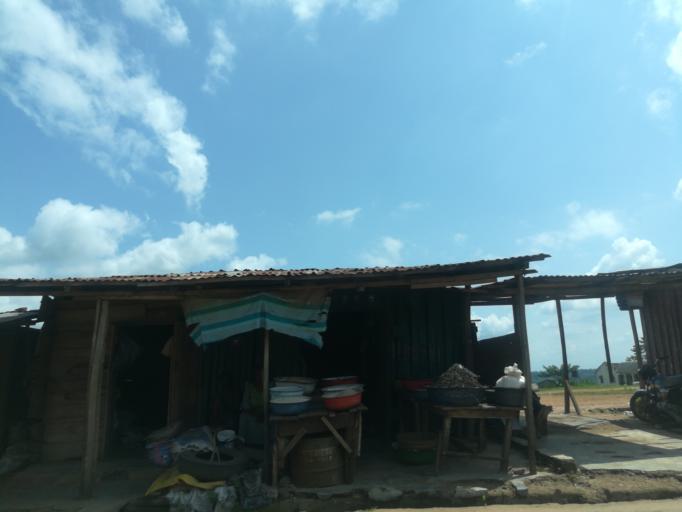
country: NG
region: Oyo
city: Egbeda
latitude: 7.4275
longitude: 4.0067
